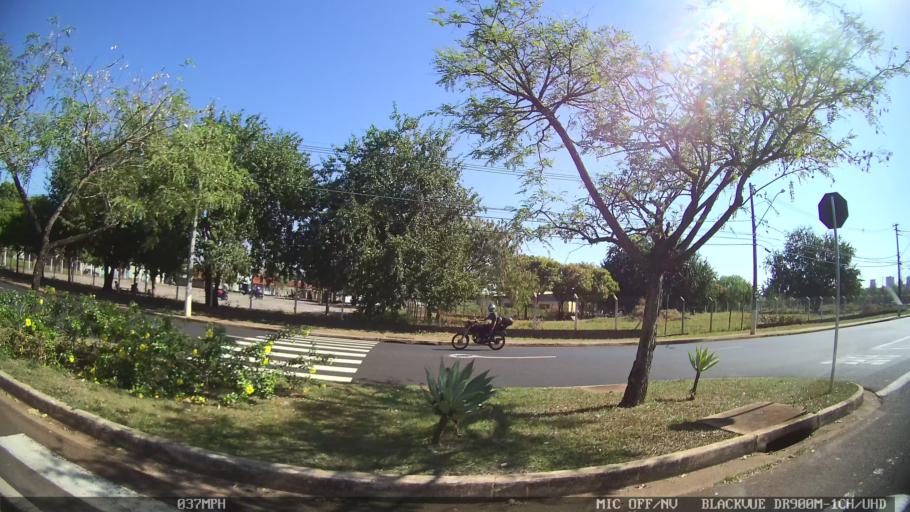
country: BR
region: Sao Paulo
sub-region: Ribeirao Preto
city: Ribeirao Preto
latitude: -21.2148
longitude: -47.7635
